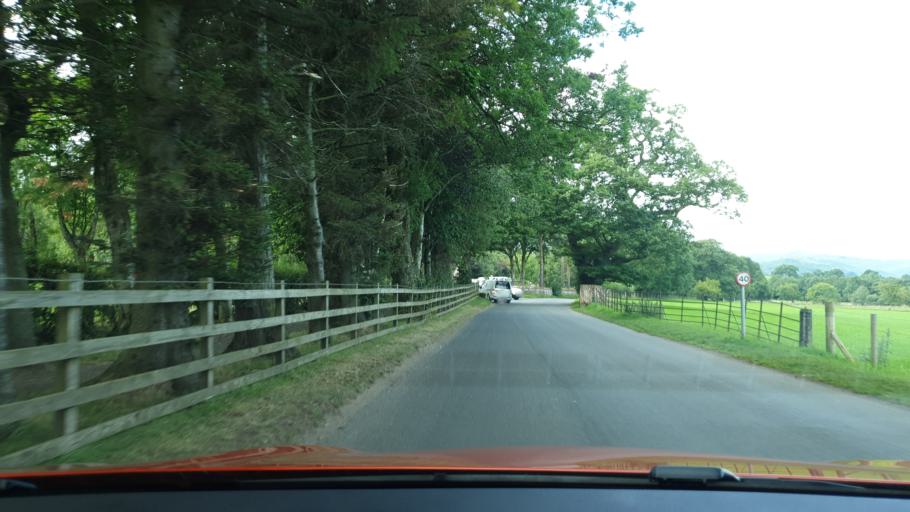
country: GB
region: England
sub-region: Cumbria
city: Penrith
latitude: 54.6040
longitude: -2.8237
